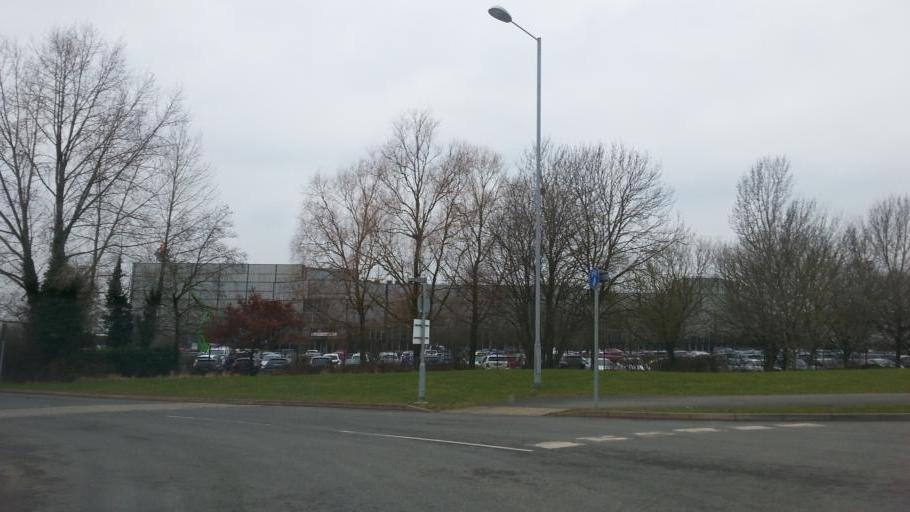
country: GB
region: England
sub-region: Northamptonshire
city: Corby
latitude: 52.5064
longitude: -0.6429
